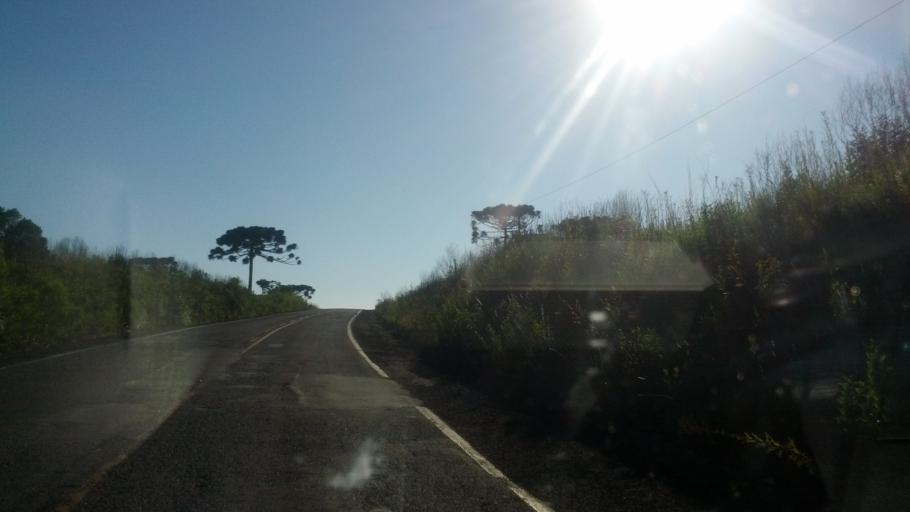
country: BR
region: Santa Catarina
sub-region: Lages
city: Lages
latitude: -27.9144
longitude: -50.5891
